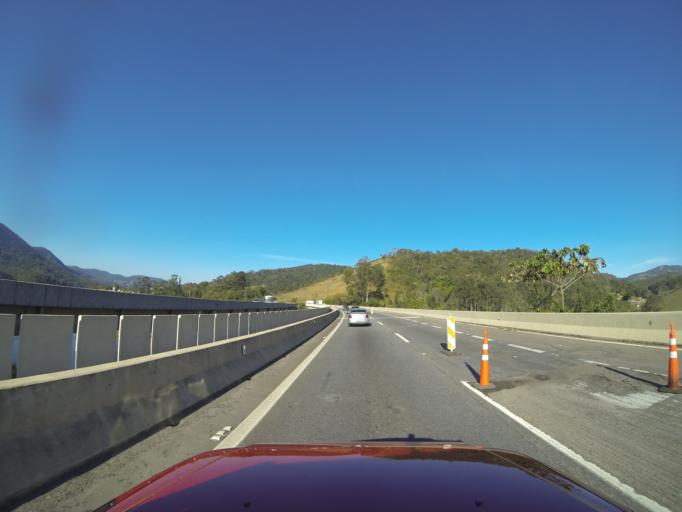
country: BR
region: Sao Paulo
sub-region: Bom Jesus Dos Perdoes
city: Bom Jesus dos Perdoes
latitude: -23.1939
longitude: -46.3474
